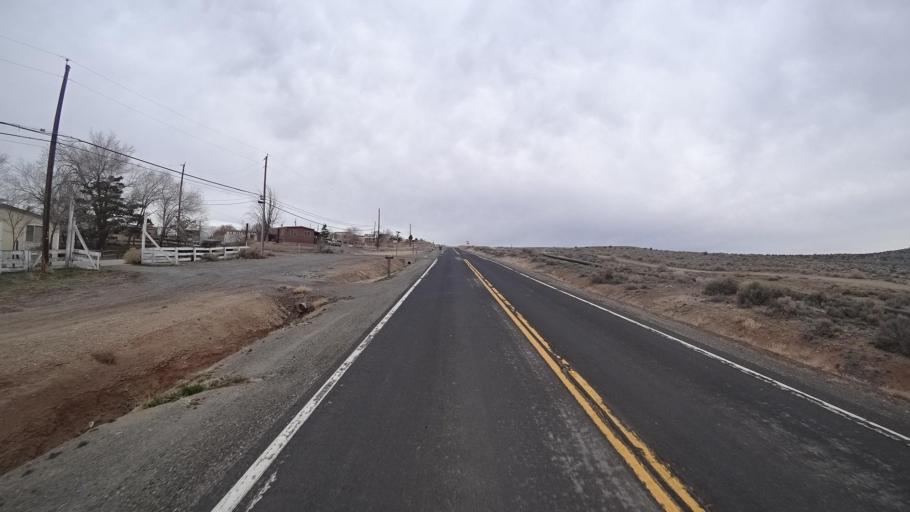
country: US
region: Nevada
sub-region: Washoe County
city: Lemmon Valley
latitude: 39.6749
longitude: -119.8515
